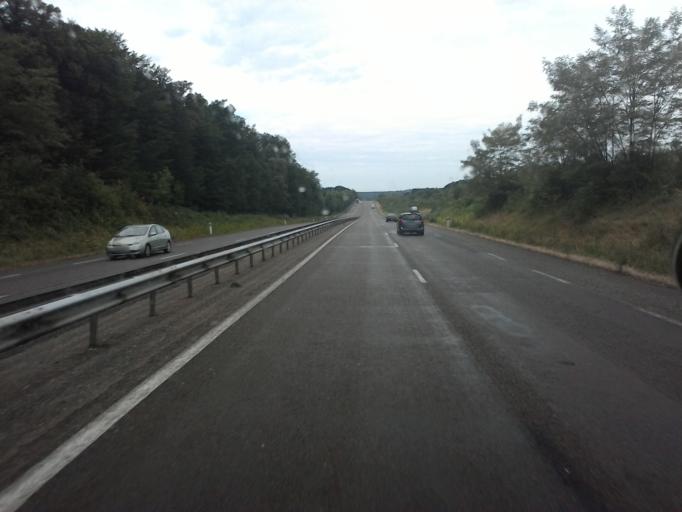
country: FR
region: Franche-Comte
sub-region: Departement du Jura
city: Poligny
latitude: 46.8409
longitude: 5.6691
